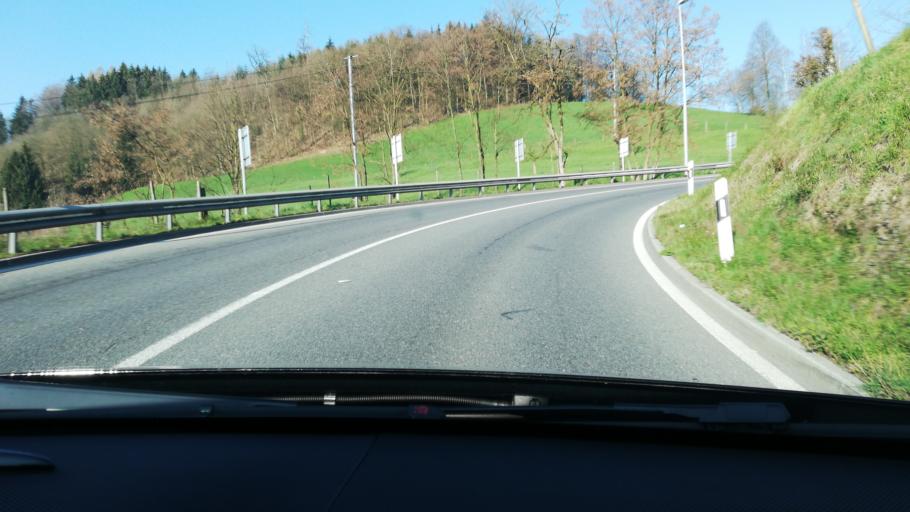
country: CH
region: Lucerne
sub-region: Lucerne-Stadt District
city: Luzern
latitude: 47.0647
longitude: 8.2978
